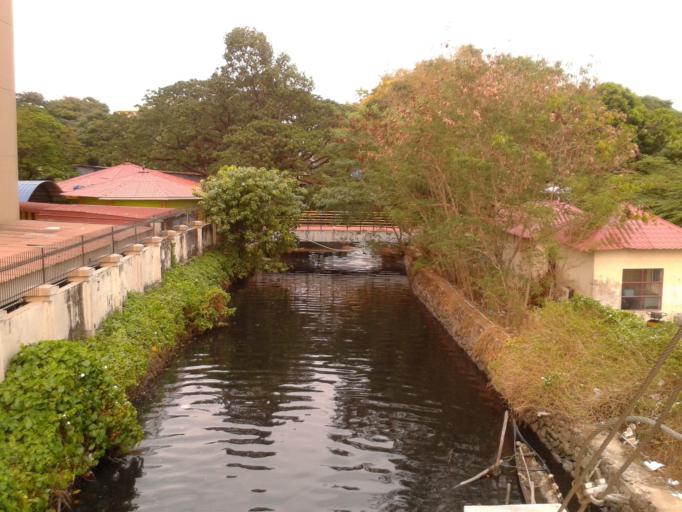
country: IN
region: Kerala
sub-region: Ernakulam
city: Cochin
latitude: 9.9746
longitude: 76.2774
